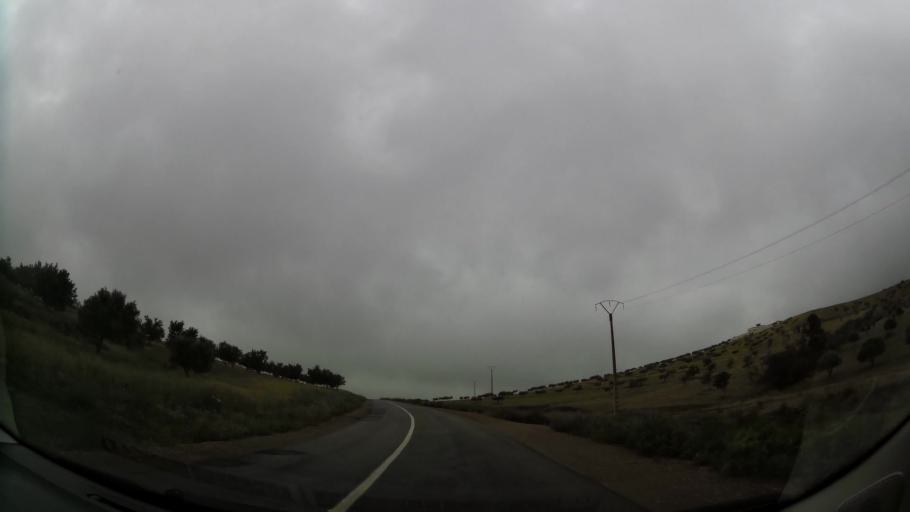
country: MA
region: Oriental
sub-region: Nador
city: Selouane
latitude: 35.1216
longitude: -3.0628
